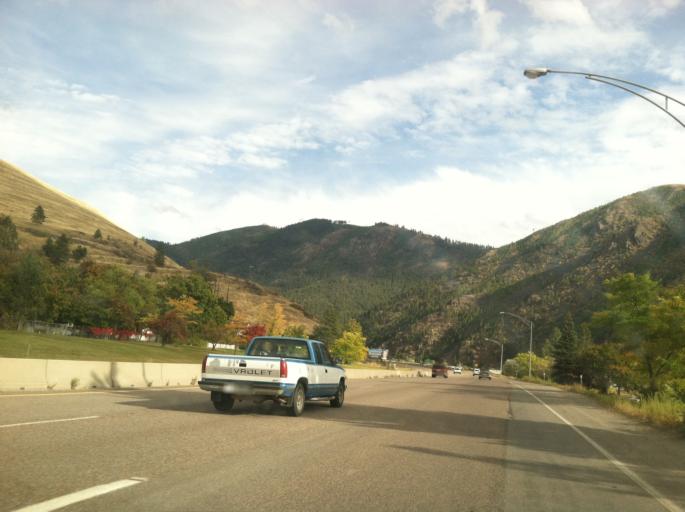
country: US
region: Montana
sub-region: Missoula County
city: Missoula
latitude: 46.8685
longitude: -113.9787
